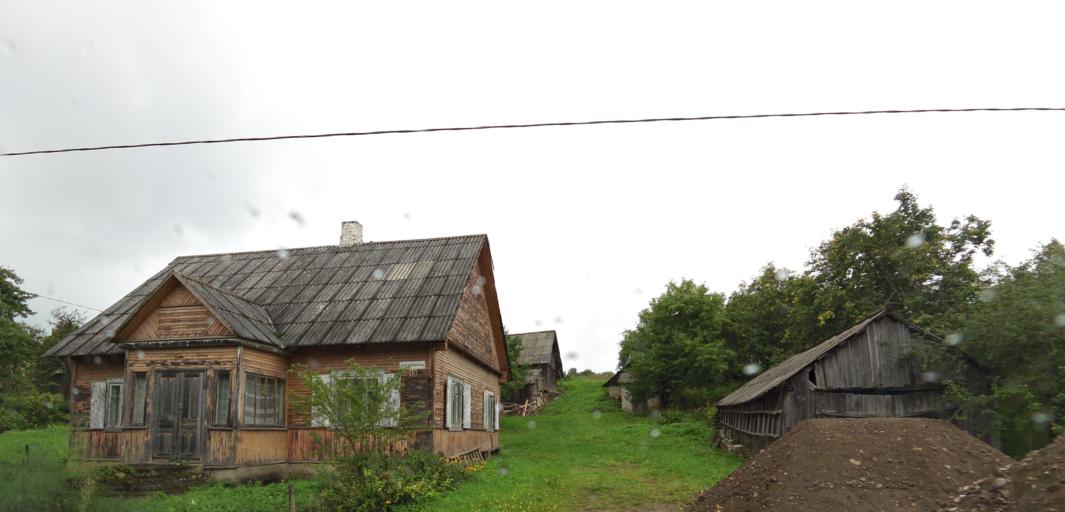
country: LT
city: Sirvintos
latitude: 55.0745
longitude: 25.0640
